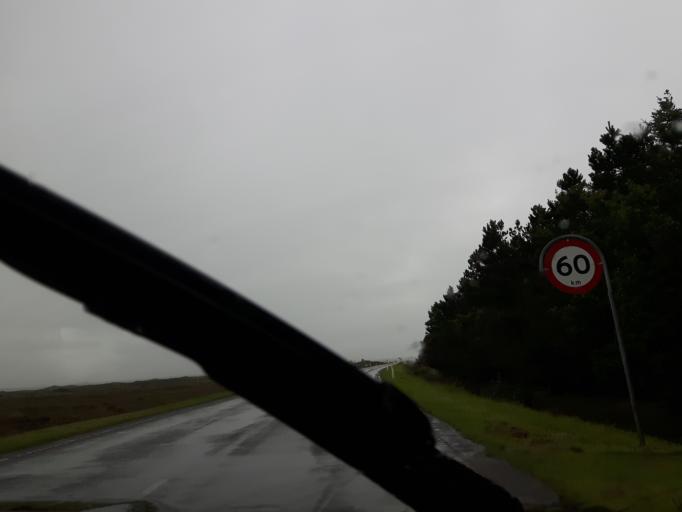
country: DK
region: North Denmark
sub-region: Thisted Kommune
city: Hanstholm
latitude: 57.0038
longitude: 8.4664
